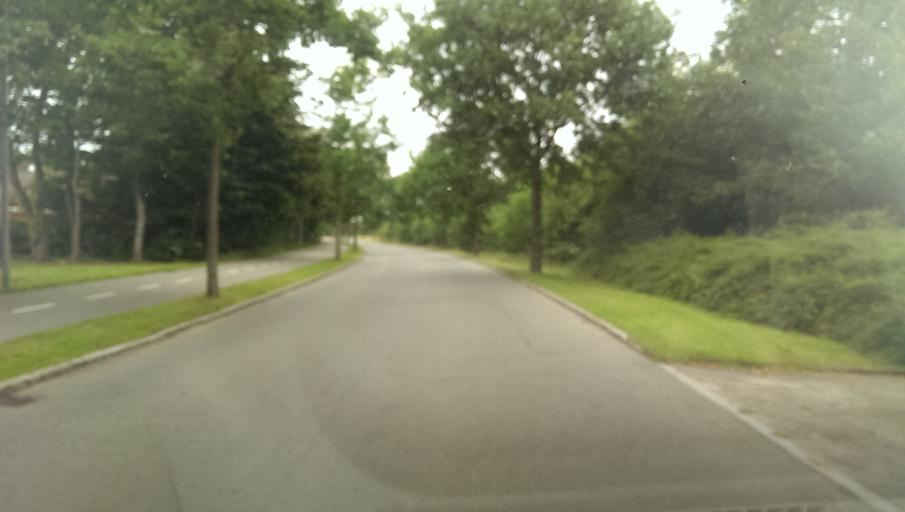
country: DK
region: South Denmark
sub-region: Esbjerg Kommune
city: Bramming
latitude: 55.4726
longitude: 8.7150
